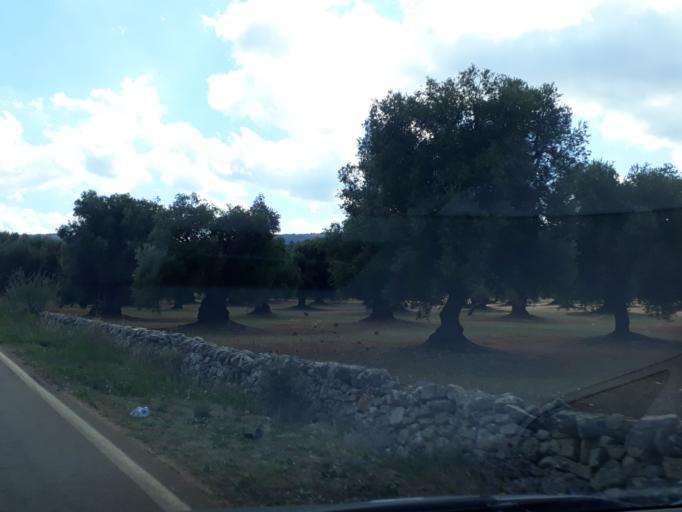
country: IT
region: Apulia
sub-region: Provincia di Brindisi
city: Pezze di Greco
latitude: 40.8087
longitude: 17.3879
